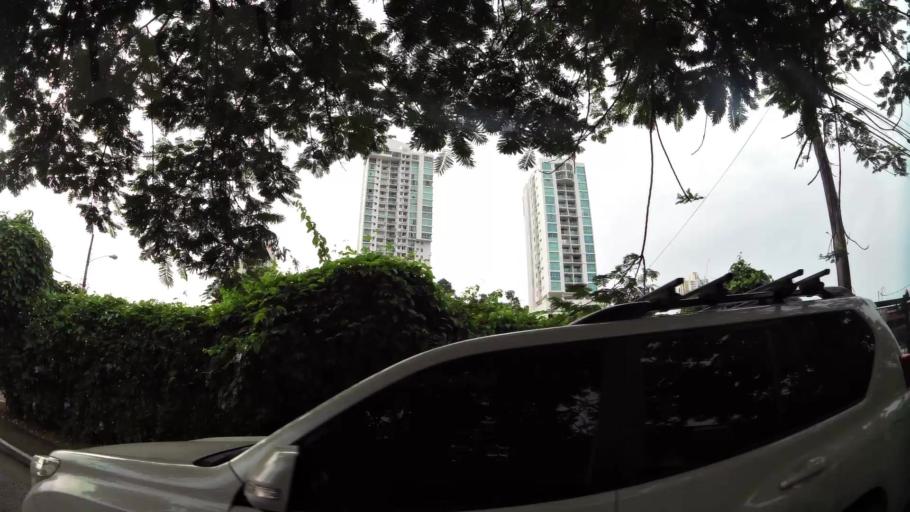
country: PA
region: Panama
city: Panama
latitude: 9.0091
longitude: -79.5107
